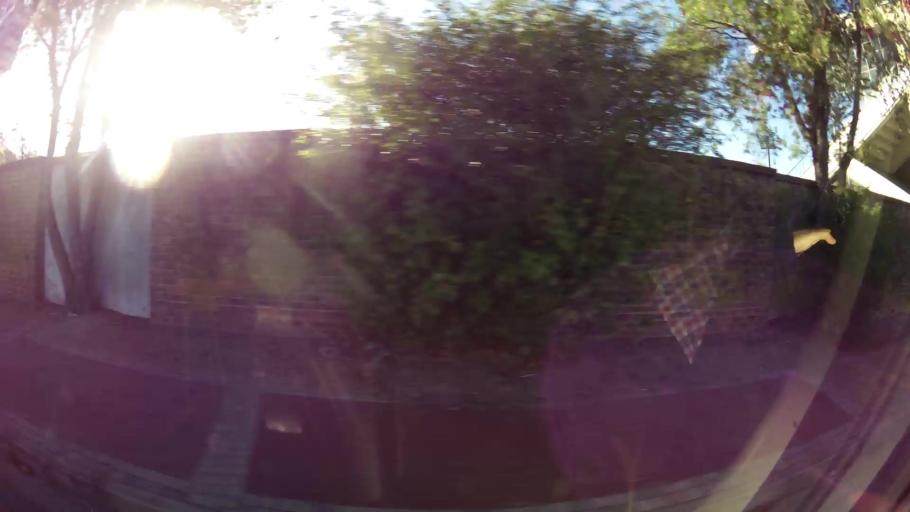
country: ZA
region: Western Cape
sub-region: Eden District Municipality
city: George
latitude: -33.9528
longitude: 22.4469
